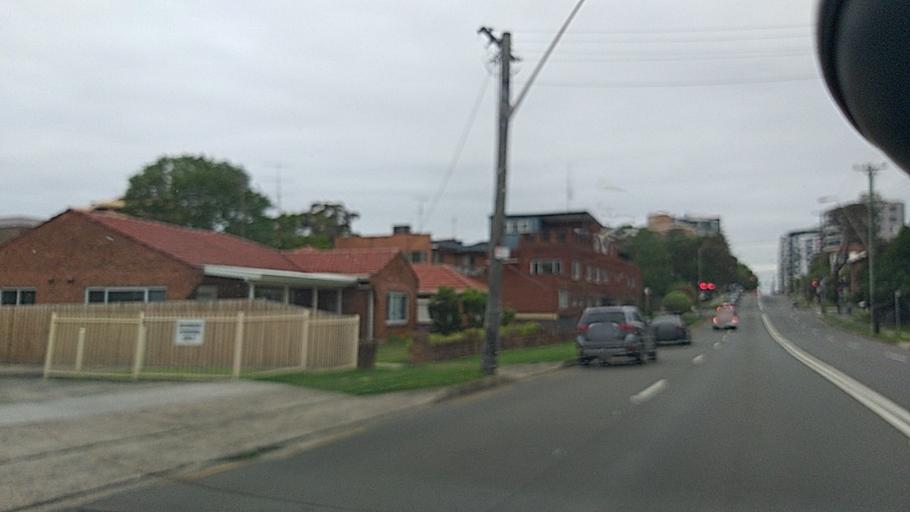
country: AU
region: New South Wales
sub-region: Wollongong
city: Wollongong
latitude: -34.4214
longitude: 150.9008
